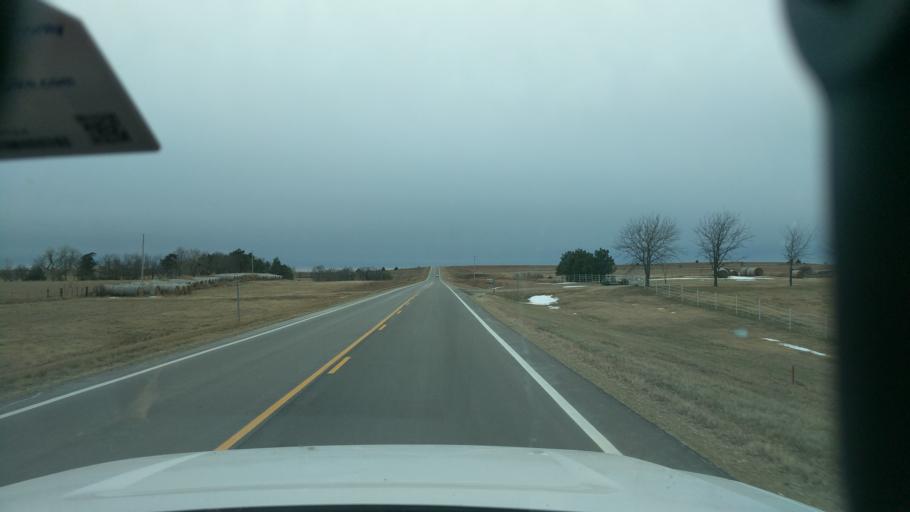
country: US
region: Kansas
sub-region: Dickinson County
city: Herington
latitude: 38.7174
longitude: -96.9279
